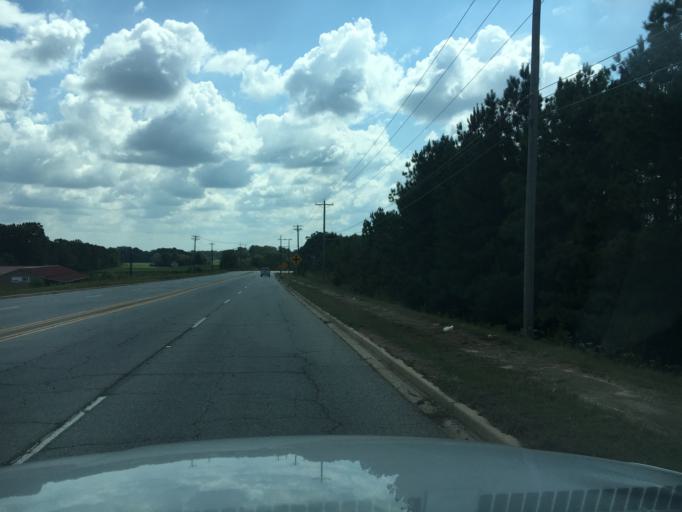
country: US
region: South Carolina
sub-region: Greenwood County
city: Greenwood
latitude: 34.1772
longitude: -82.1836
